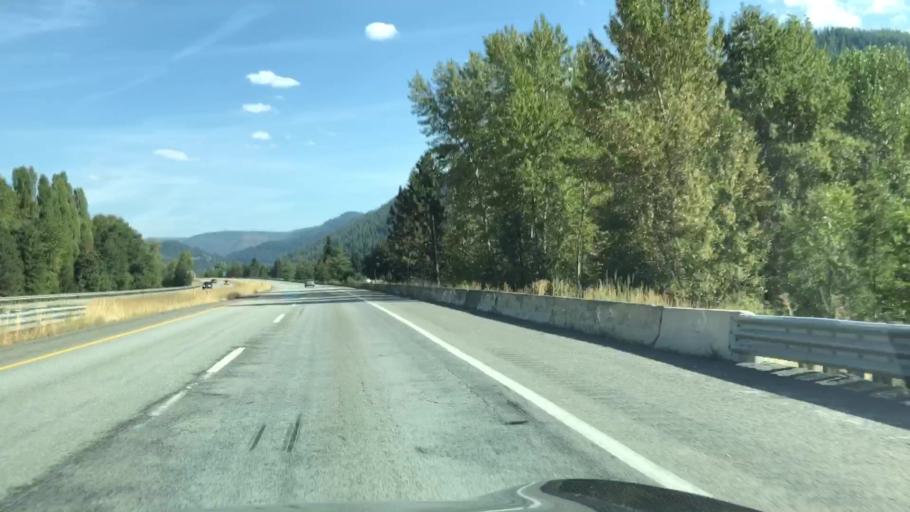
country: US
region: Idaho
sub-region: Shoshone County
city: Osburn
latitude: 47.5164
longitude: -116.0330
